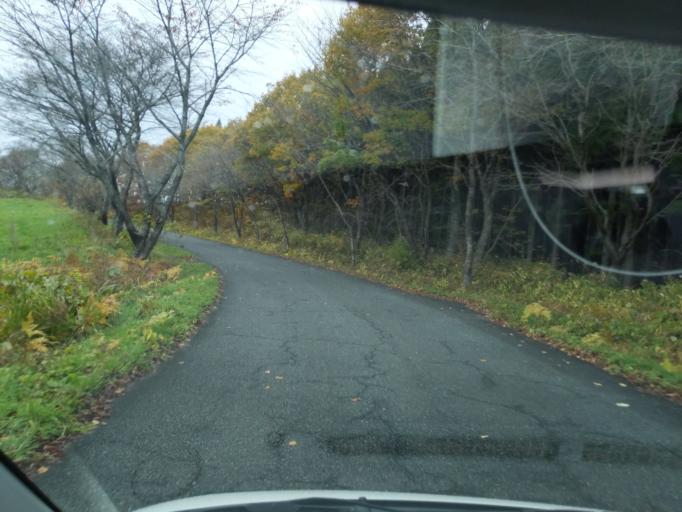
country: JP
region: Iwate
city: Mizusawa
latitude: 39.0700
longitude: 141.0397
